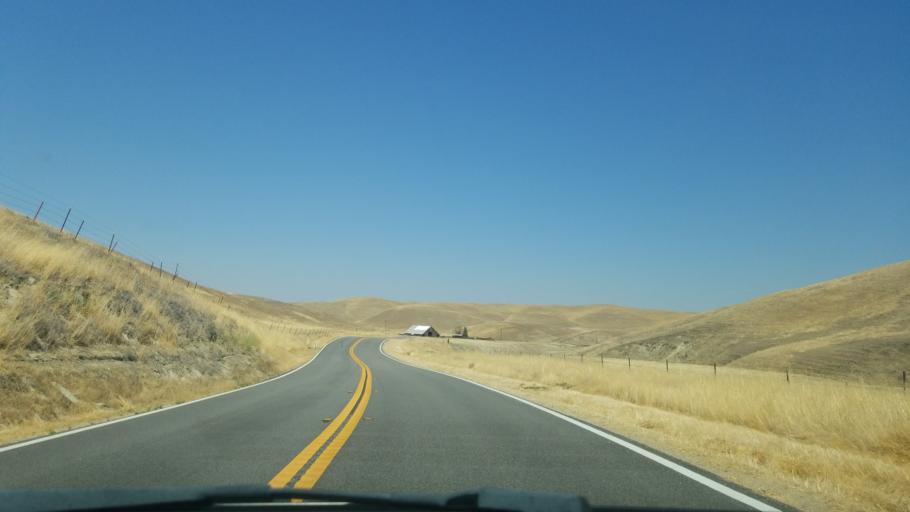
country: US
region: California
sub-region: San Luis Obispo County
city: Shandon
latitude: 35.5803
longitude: -120.4328
